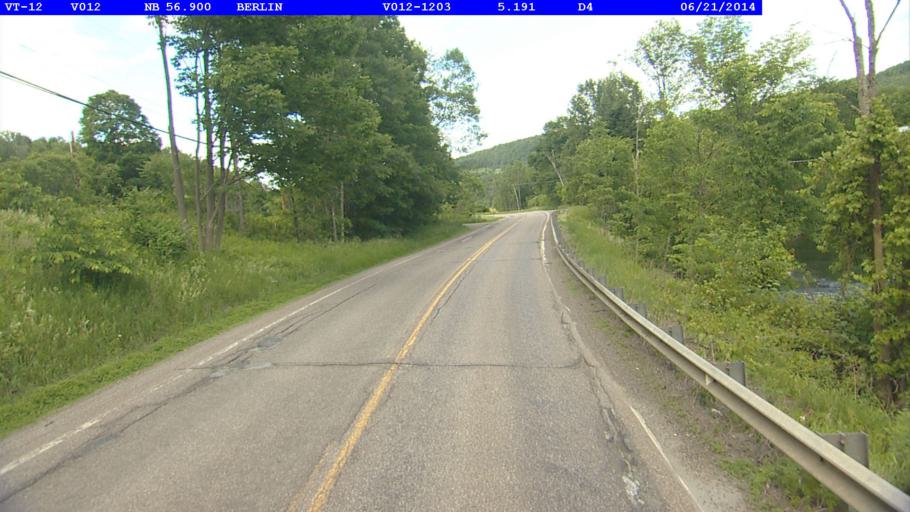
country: US
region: Vermont
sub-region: Washington County
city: Montpelier
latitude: 44.2296
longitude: -72.6036
